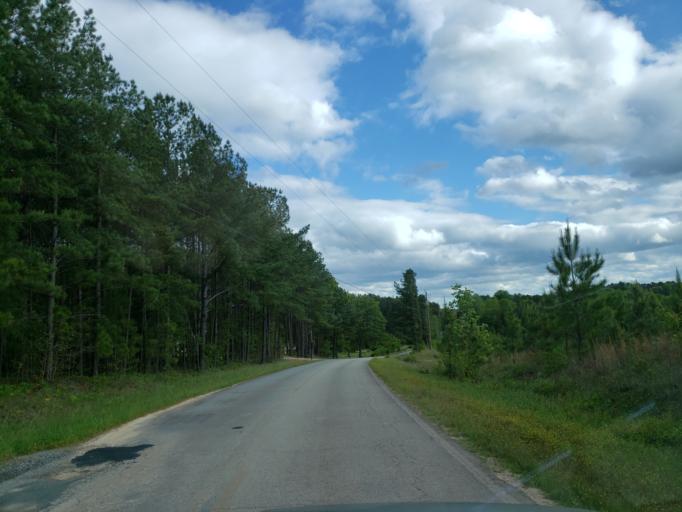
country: US
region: Georgia
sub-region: Haralson County
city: Tallapoosa
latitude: 33.8076
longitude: -85.3608
